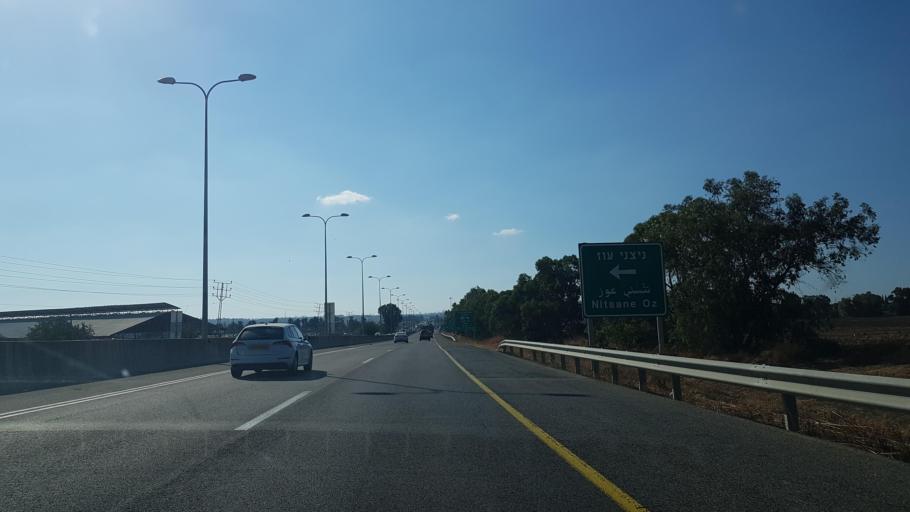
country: PS
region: West Bank
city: Tulkarm
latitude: 32.3119
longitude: 35.0059
